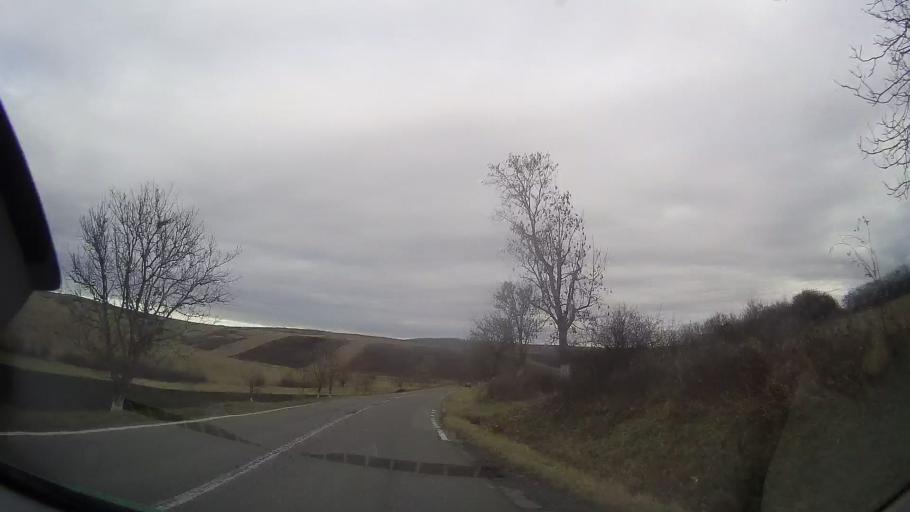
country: RO
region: Mures
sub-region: Comuna Faragau
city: Faragau
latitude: 46.7611
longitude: 24.5413
